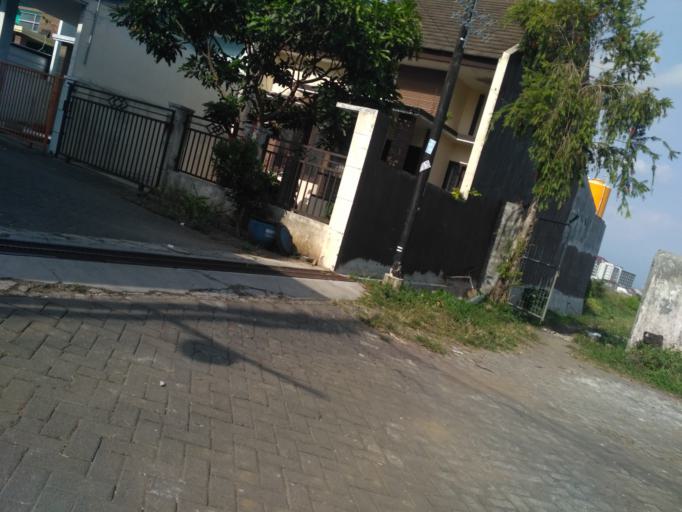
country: ID
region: East Java
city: Malang
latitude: -7.9374
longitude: 112.6133
